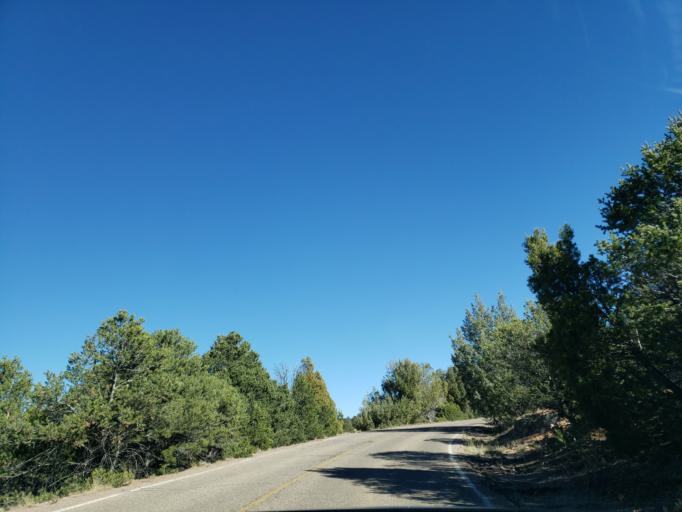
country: US
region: Colorado
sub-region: Fremont County
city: Canon City
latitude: 38.4638
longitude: -105.3165
